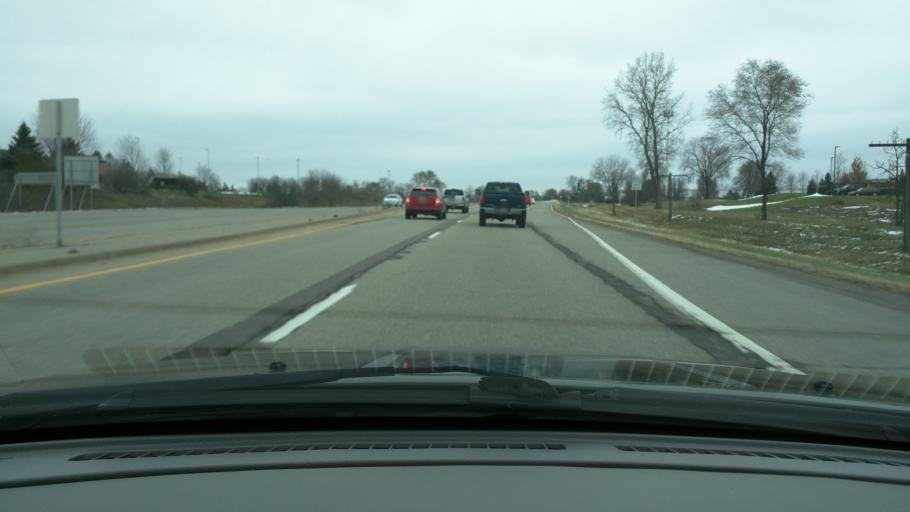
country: US
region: Minnesota
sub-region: Dakota County
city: Mendota Heights
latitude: 44.8651
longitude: -93.1533
